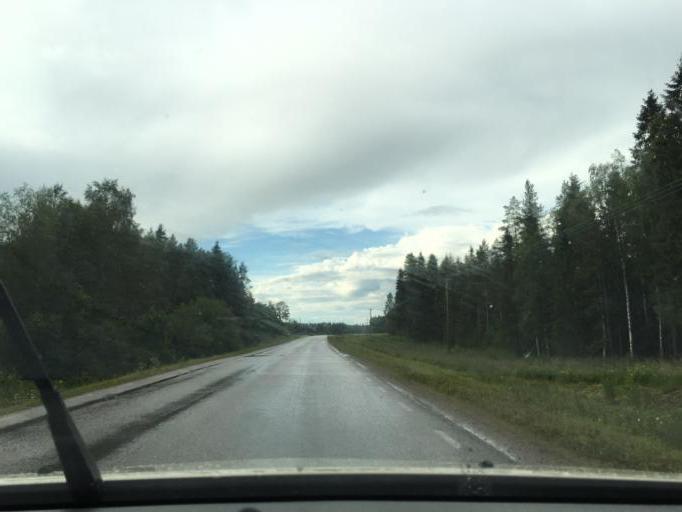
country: SE
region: Norrbotten
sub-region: Kalix Kommun
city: Toere
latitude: 65.9653
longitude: 22.8745
